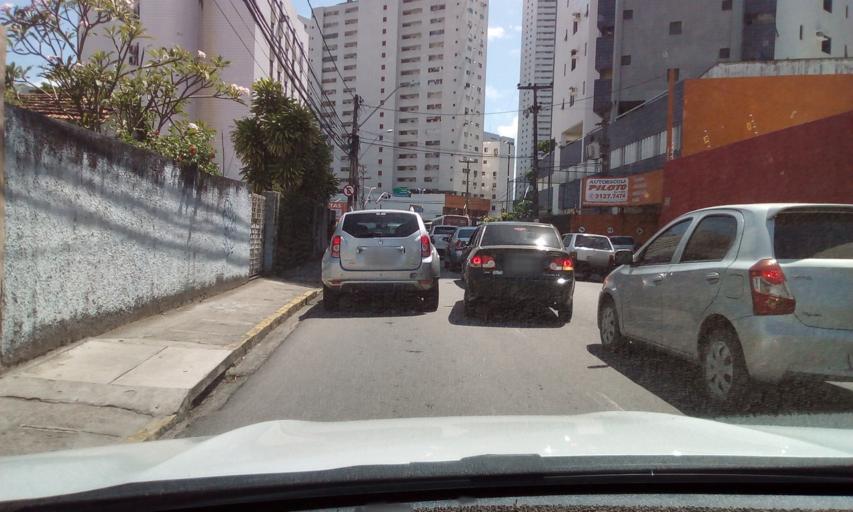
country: BR
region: Pernambuco
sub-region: Recife
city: Recife
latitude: -8.1334
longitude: -34.9037
